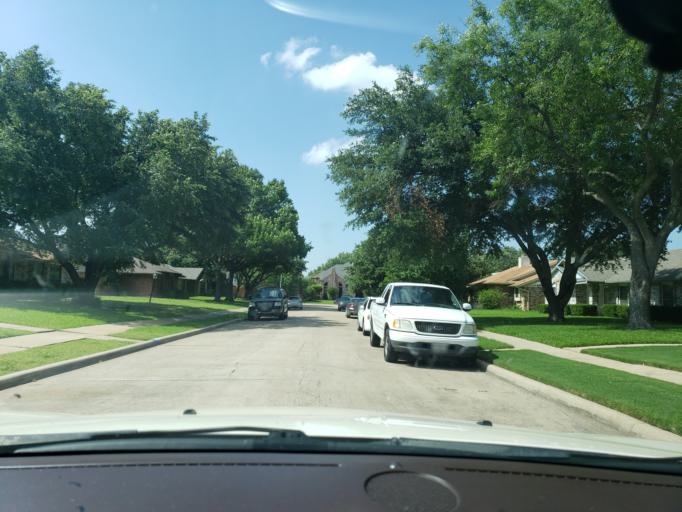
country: US
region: Texas
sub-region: Dallas County
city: Rowlett
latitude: 32.8960
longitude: -96.5751
